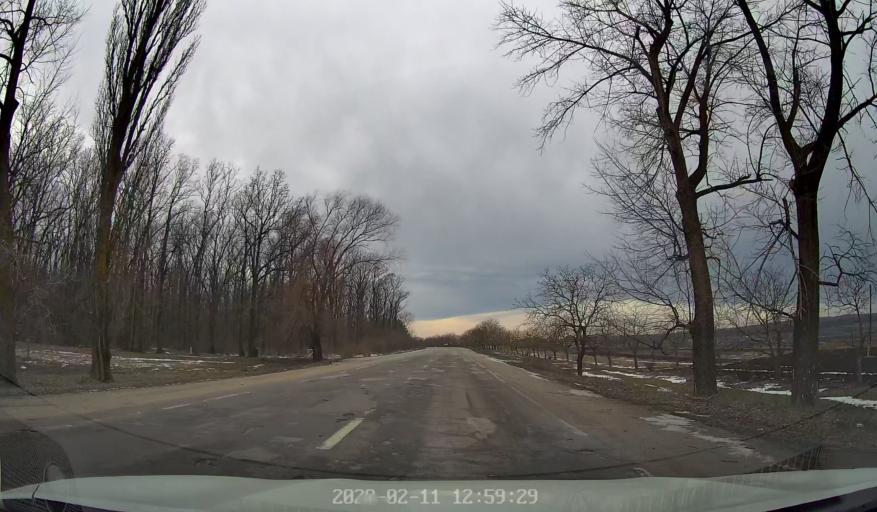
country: MD
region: Briceni
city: Briceni
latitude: 48.3287
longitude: 27.0340
